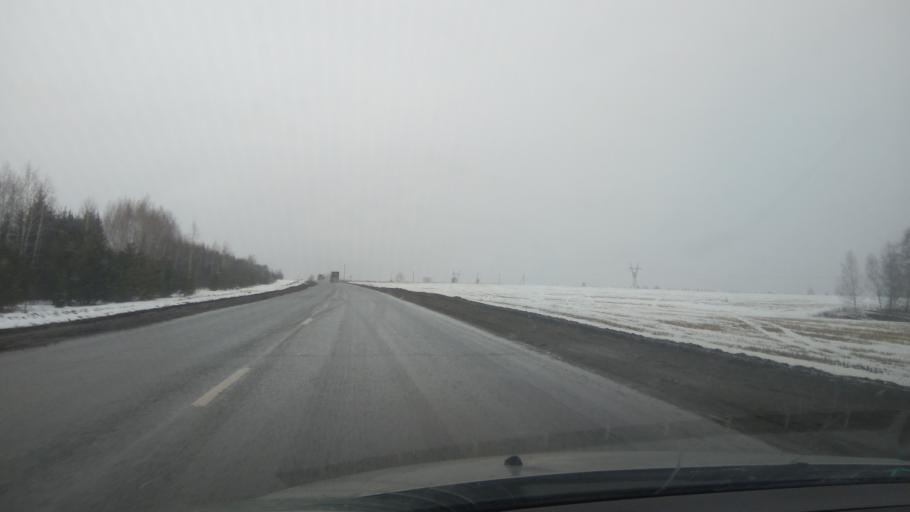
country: RU
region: Perm
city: Kungur
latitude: 57.3931
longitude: 56.9017
